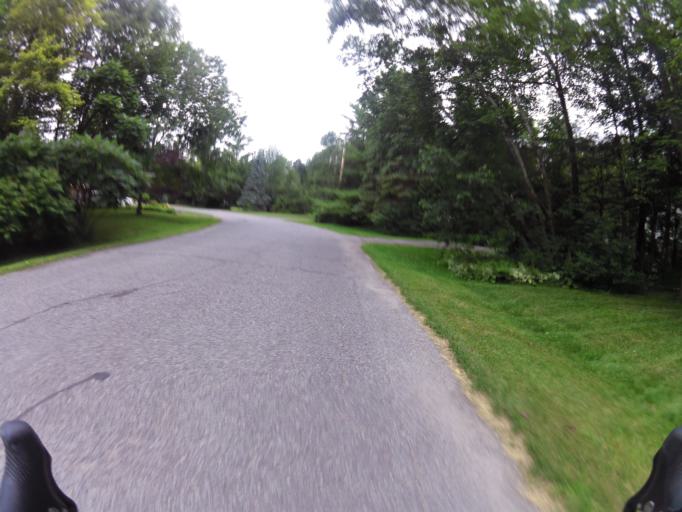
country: CA
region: Ontario
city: Ottawa
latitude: 45.3233
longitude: -75.7108
